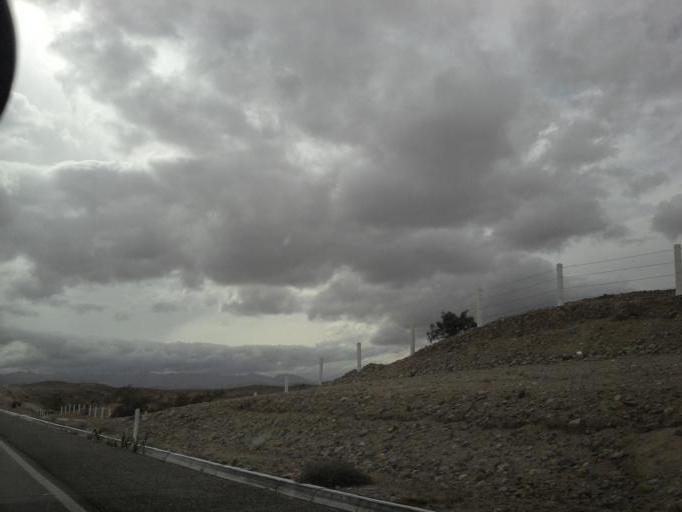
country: MX
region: Baja California
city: Progreso
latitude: 32.5674
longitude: -115.8512
